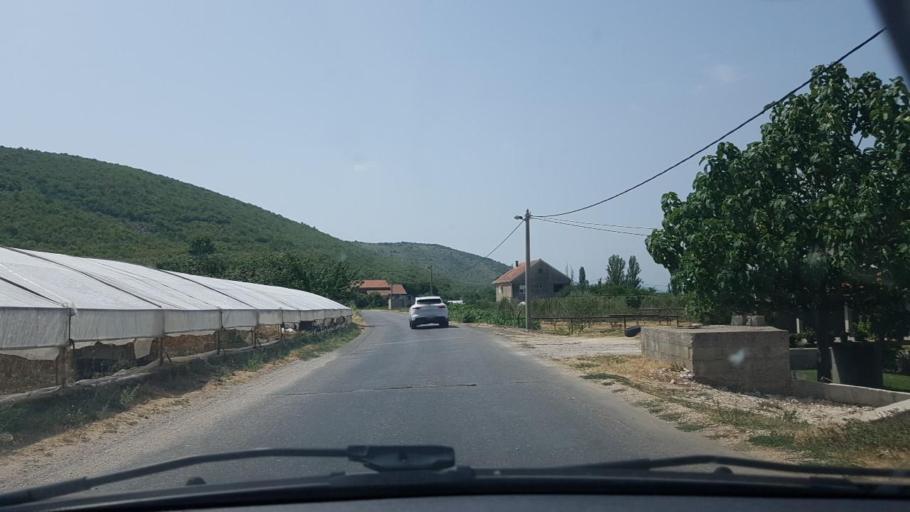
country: BA
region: Federation of Bosnia and Herzegovina
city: Tasovcici
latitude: 43.0339
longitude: 17.7308
